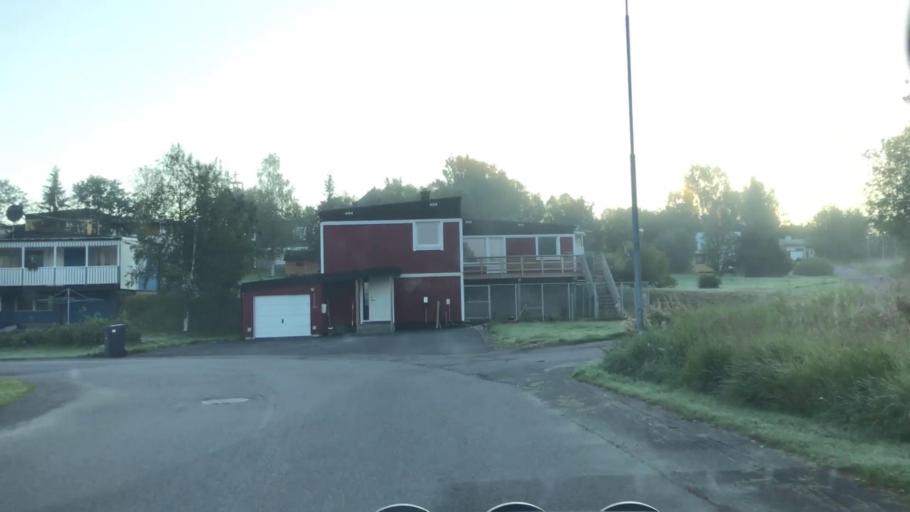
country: SE
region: Norrbotten
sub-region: Gallivare Kommun
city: Malmberget
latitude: 67.6472
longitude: 21.0489
